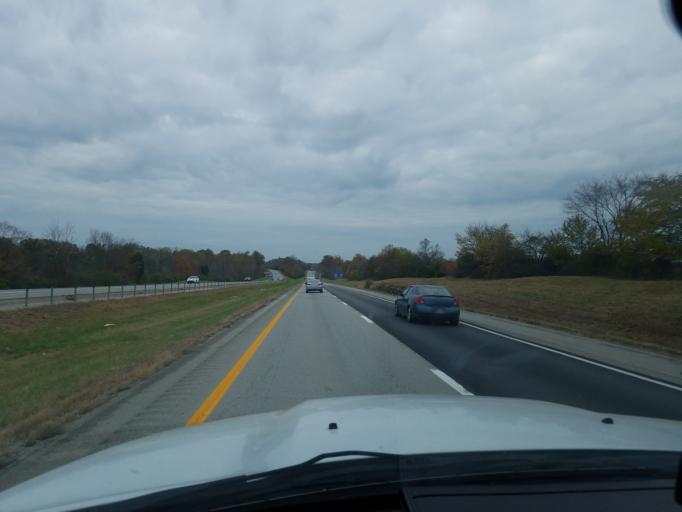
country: US
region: Kentucky
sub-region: Oldham County
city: La Grange
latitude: 38.4078
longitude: -85.3577
